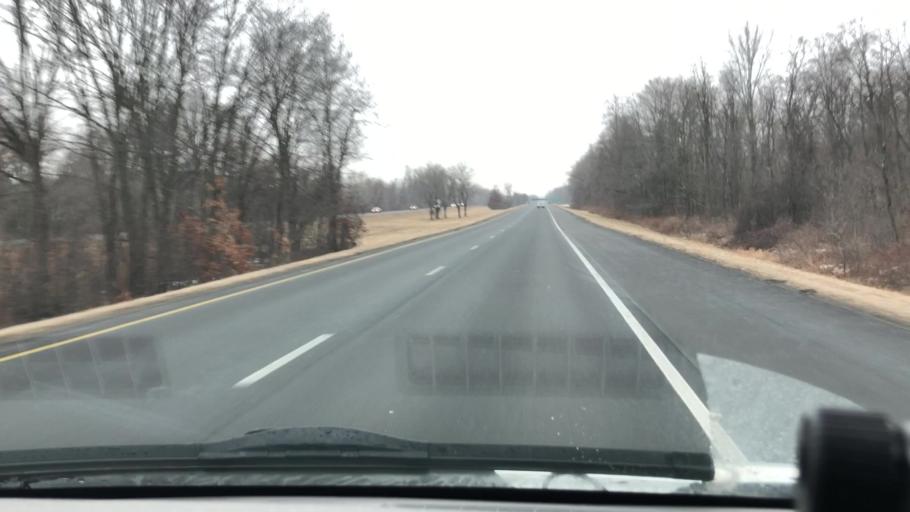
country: US
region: Massachusetts
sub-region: Franklin County
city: Whately
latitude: 42.4188
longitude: -72.6249
